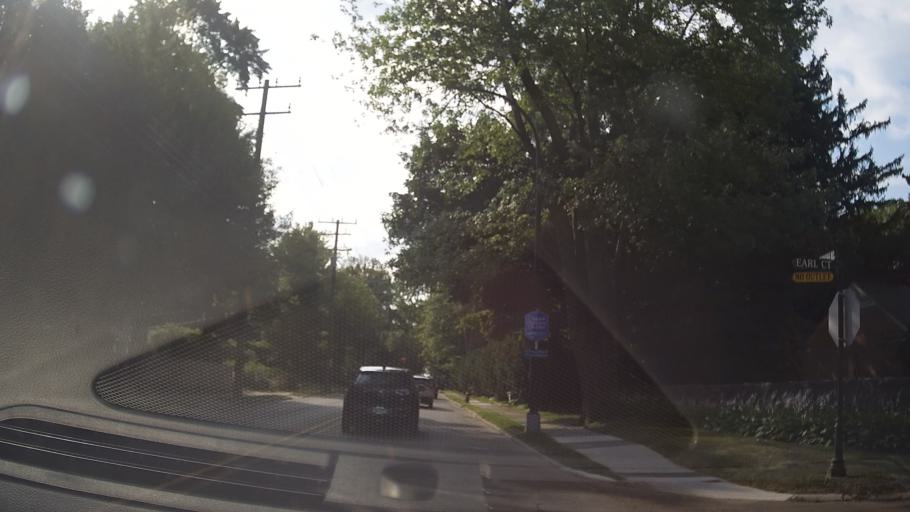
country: US
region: Michigan
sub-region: Wayne County
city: Grosse Pointe Farms
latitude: 42.4101
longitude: -82.8938
